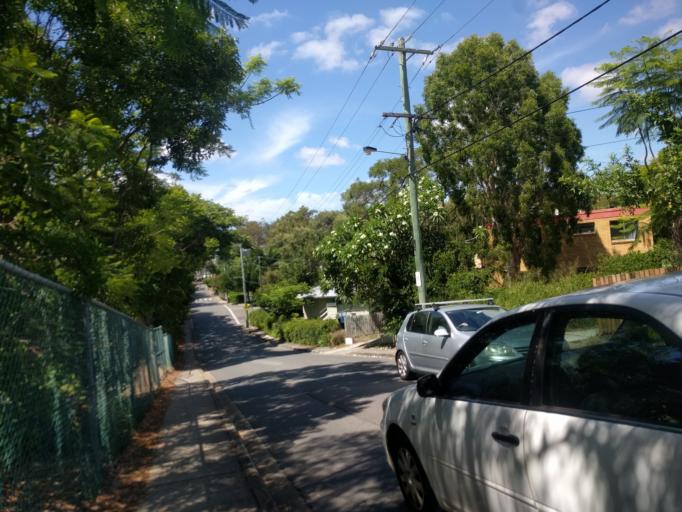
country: AU
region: Queensland
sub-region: Brisbane
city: Milton
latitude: -27.4763
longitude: 152.9966
